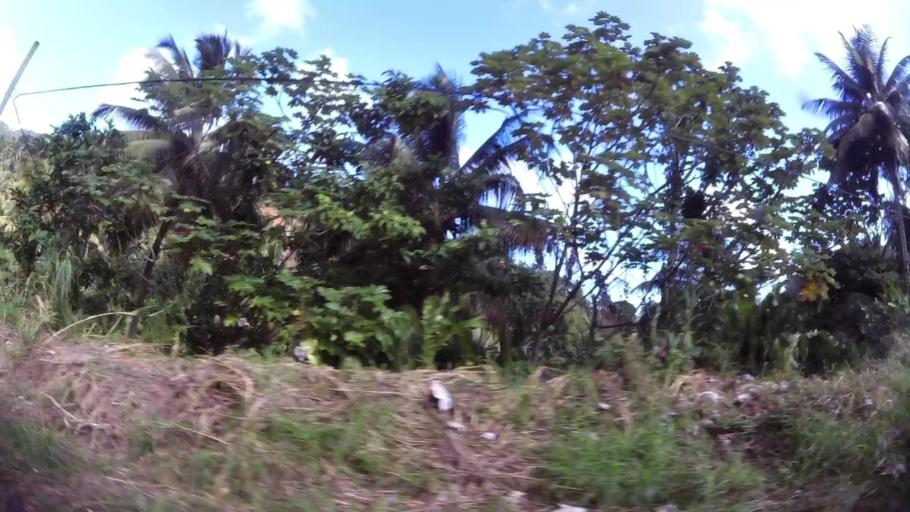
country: DM
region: Saint David
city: Castle Bruce
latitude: 15.4733
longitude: -61.2514
